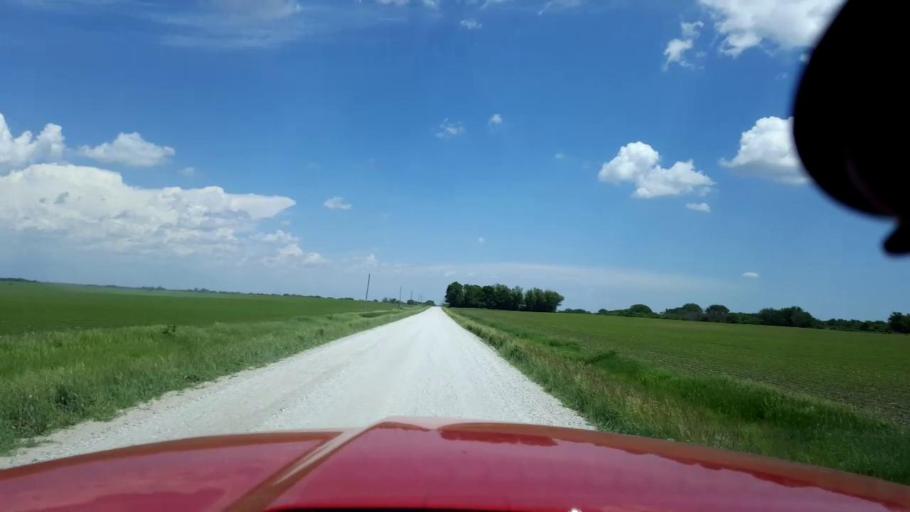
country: US
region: Iowa
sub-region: Boone County
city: Boone
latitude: 42.0493
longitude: -93.7756
